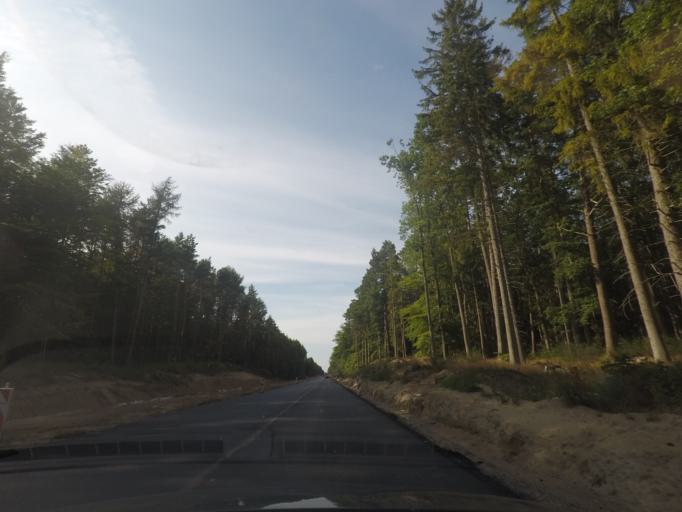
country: PL
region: Pomeranian Voivodeship
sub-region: Powiat leborski
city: Leba
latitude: 54.6982
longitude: 17.5892
